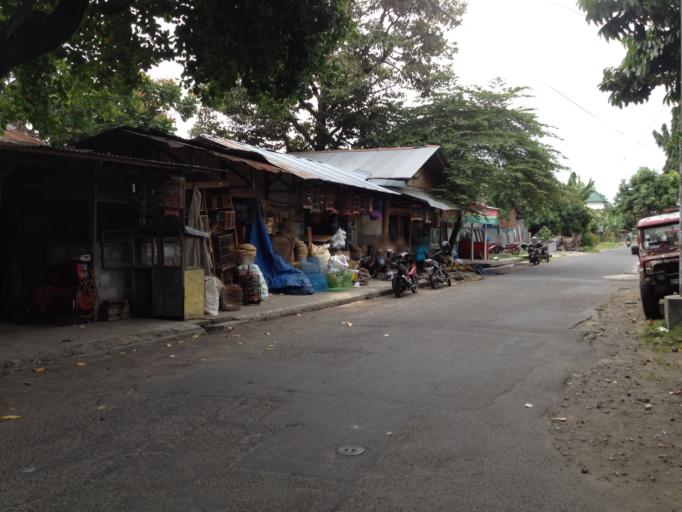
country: ID
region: Daerah Istimewa Yogyakarta
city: Yogyakarta
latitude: -7.8134
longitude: 110.3987
